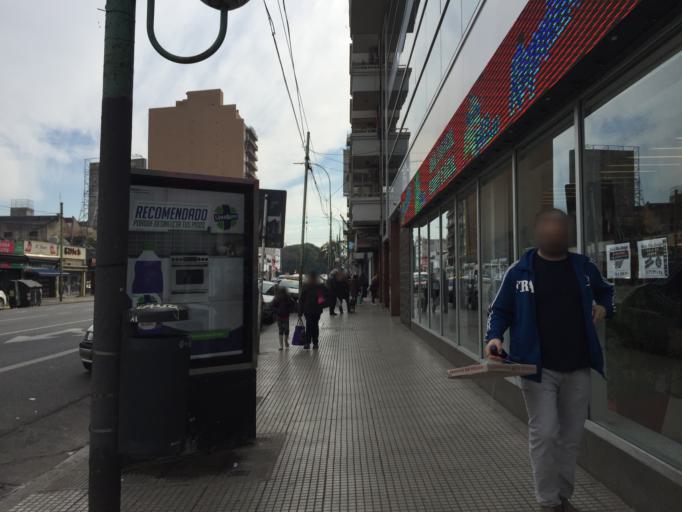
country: AR
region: Buenos Aires F.D.
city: Colegiales
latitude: -34.5932
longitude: -58.4458
